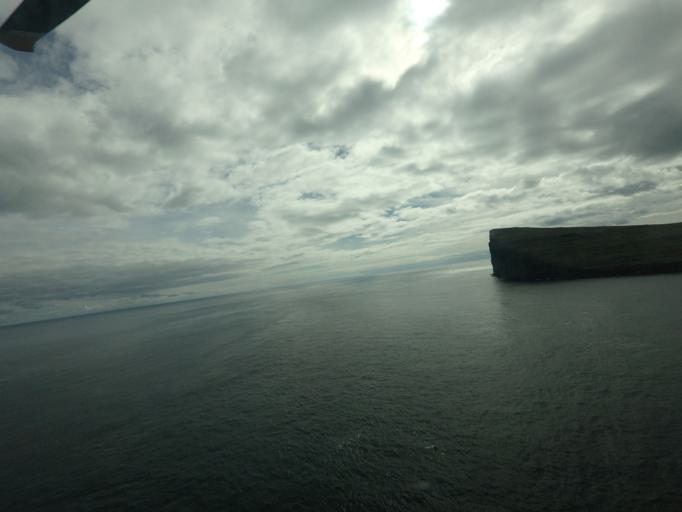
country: FO
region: Nordoyar
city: Klaksvik
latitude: 62.3099
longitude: -6.3095
